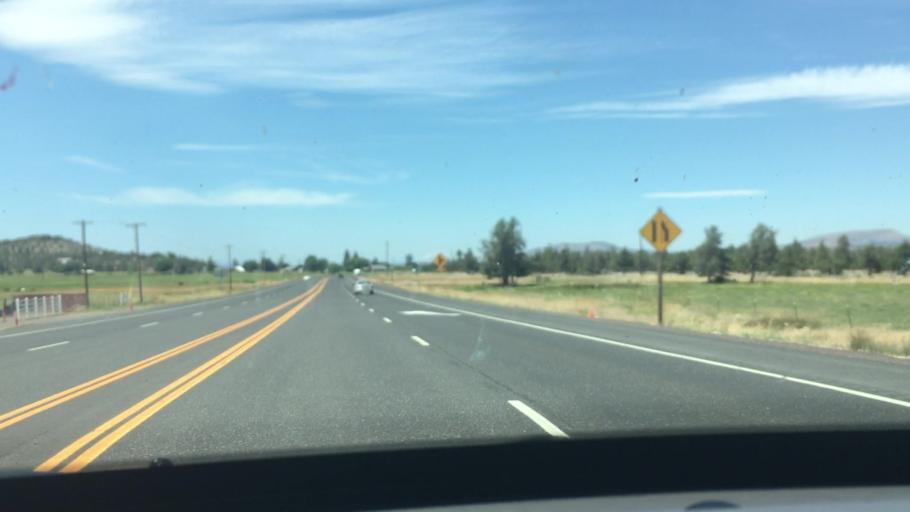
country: US
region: Oregon
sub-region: Deschutes County
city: Terrebonne
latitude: 44.3214
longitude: -121.1732
